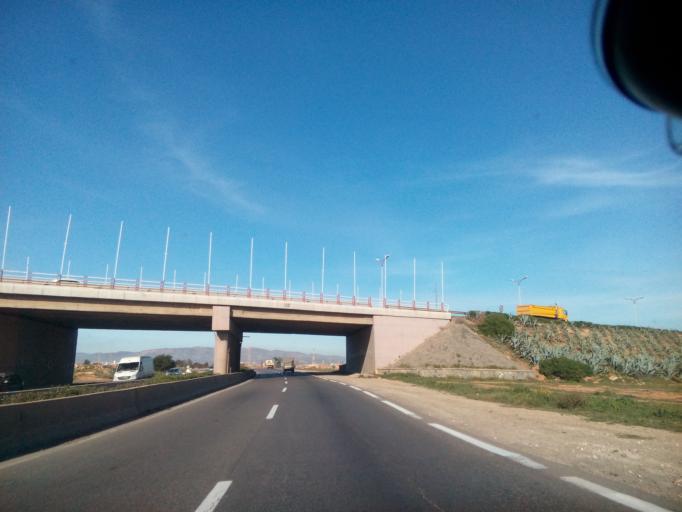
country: DZ
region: Oran
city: Ain el Bya
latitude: 35.7996
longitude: -0.2936
